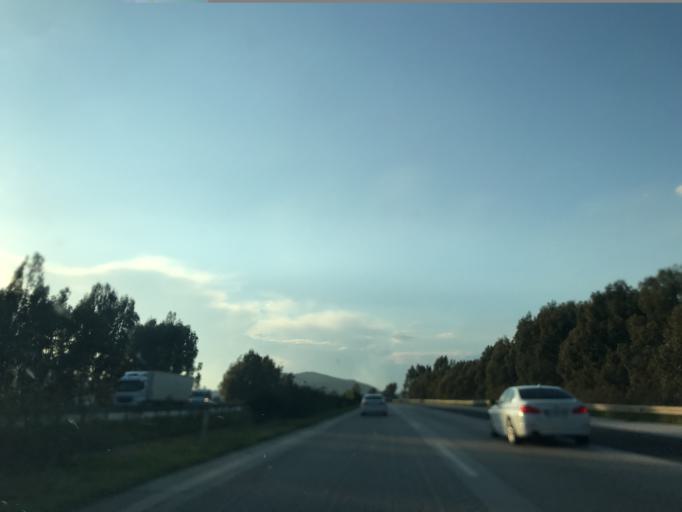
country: TR
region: Adana
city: Ceyhan
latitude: 36.9842
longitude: 35.7717
